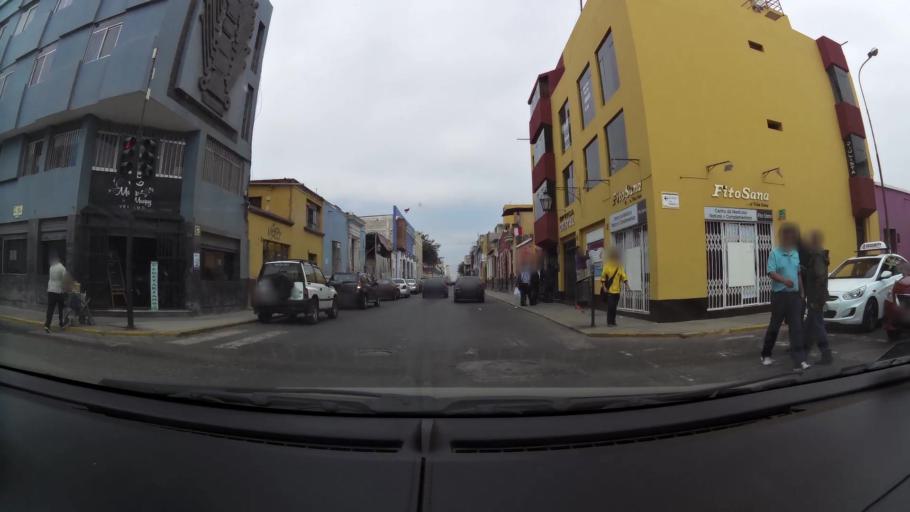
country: PE
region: La Libertad
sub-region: Provincia de Trujillo
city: Trujillo
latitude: -8.1088
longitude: -79.0285
